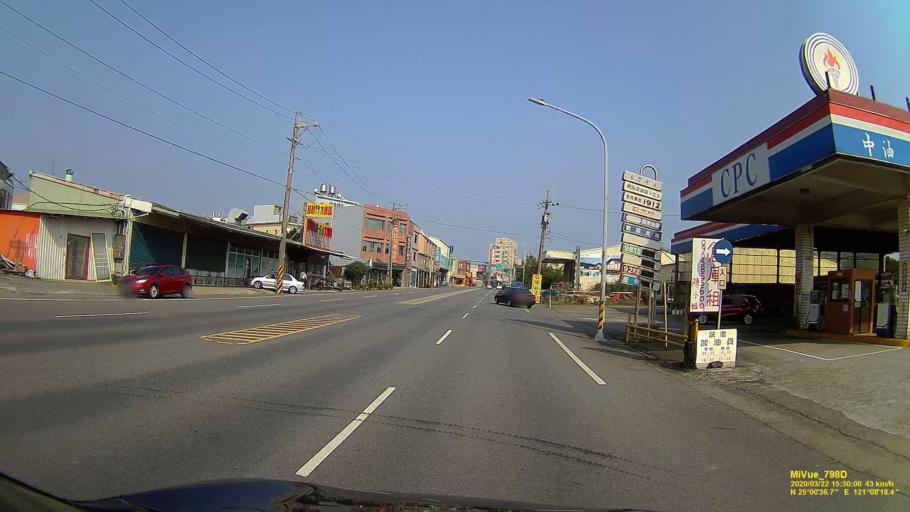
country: TW
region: Taiwan
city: Taoyuan City
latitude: 25.0101
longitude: 121.1393
